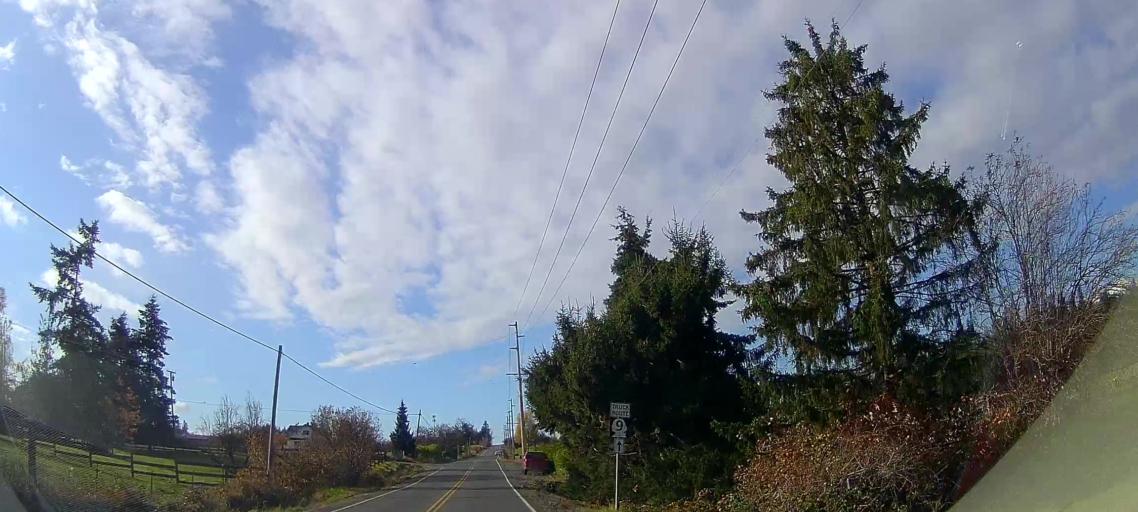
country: US
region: Washington
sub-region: Skagit County
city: Clear Lake
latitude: 48.4352
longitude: -122.2464
